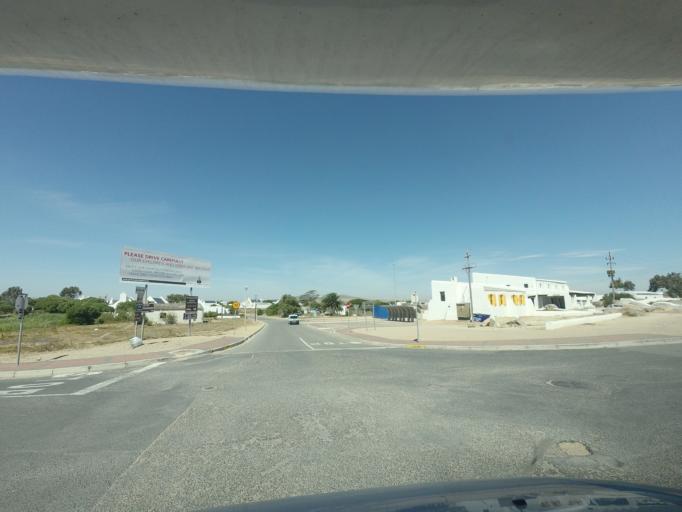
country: ZA
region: Western Cape
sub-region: West Coast District Municipality
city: Vredenburg
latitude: -32.8095
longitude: 17.8945
